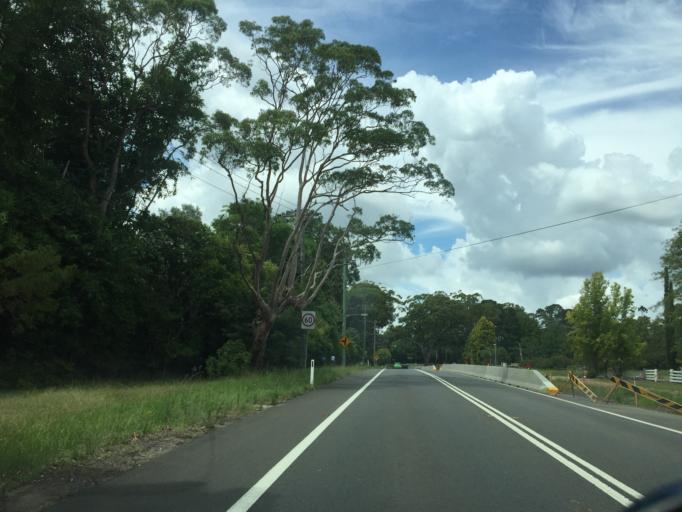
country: AU
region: New South Wales
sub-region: Hornsby Shire
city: Galston
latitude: -33.6672
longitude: 151.0375
